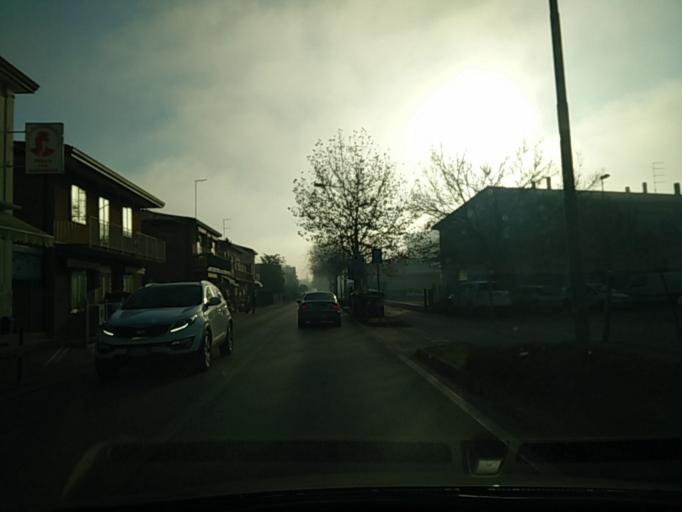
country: IT
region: Veneto
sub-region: Provincia di Padova
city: Sarmeola
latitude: 45.4246
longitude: 11.8518
